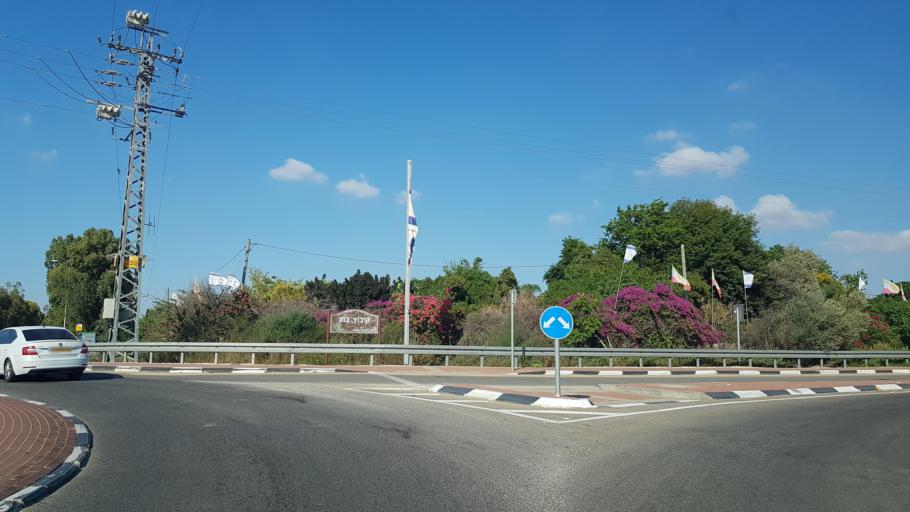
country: PS
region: West Bank
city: Tulkarm
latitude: 32.3508
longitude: 35.0137
